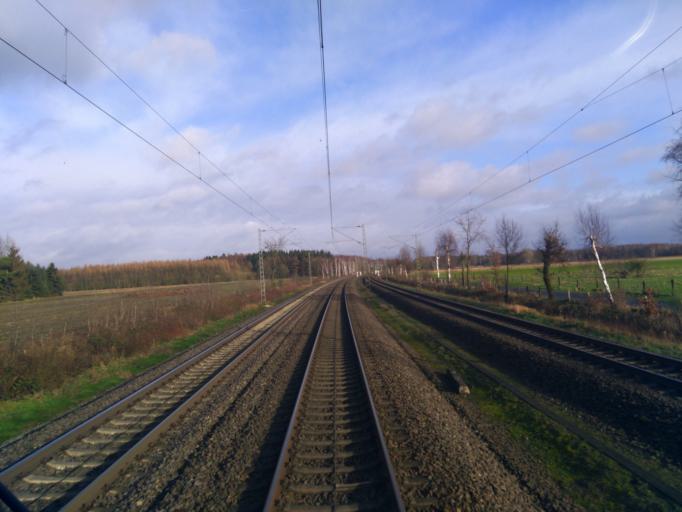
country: DE
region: Lower Saxony
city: Lauenbruck
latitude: 53.1867
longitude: 9.5275
